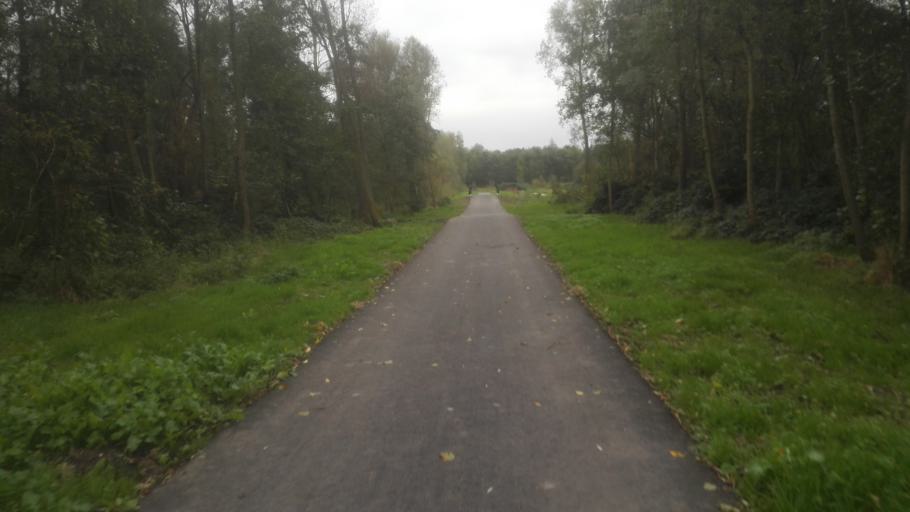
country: NL
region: South Holland
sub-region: Gemeente Delft
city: Delft
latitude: 51.9836
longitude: 4.3882
